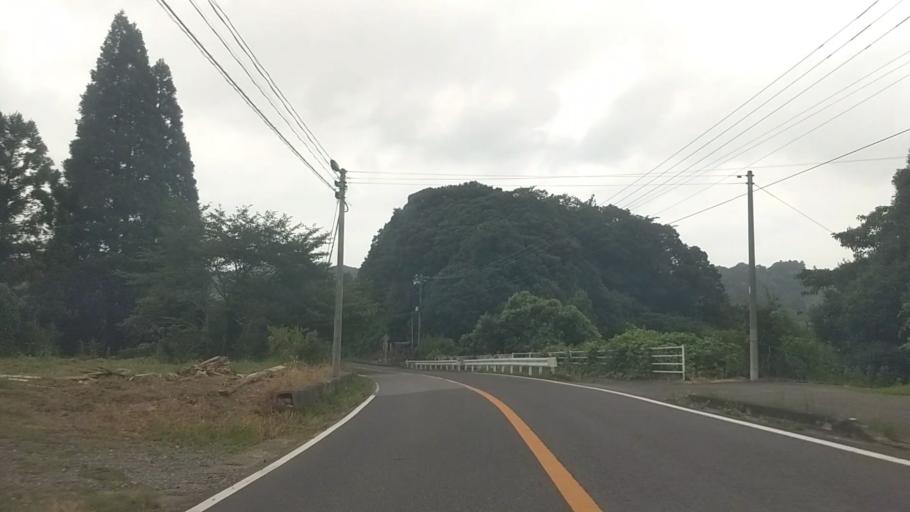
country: JP
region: Chiba
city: Katsuura
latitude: 35.2482
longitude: 140.1949
